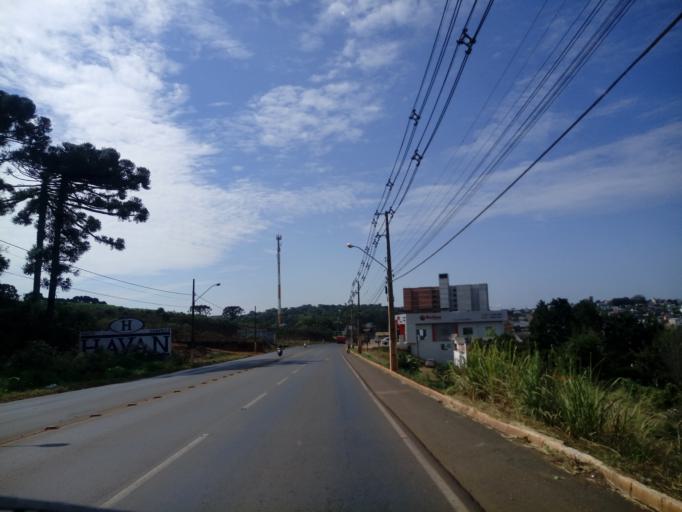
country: BR
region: Santa Catarina
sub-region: Chapeco
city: Chapeco
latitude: -27.0945
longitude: -52.6902
